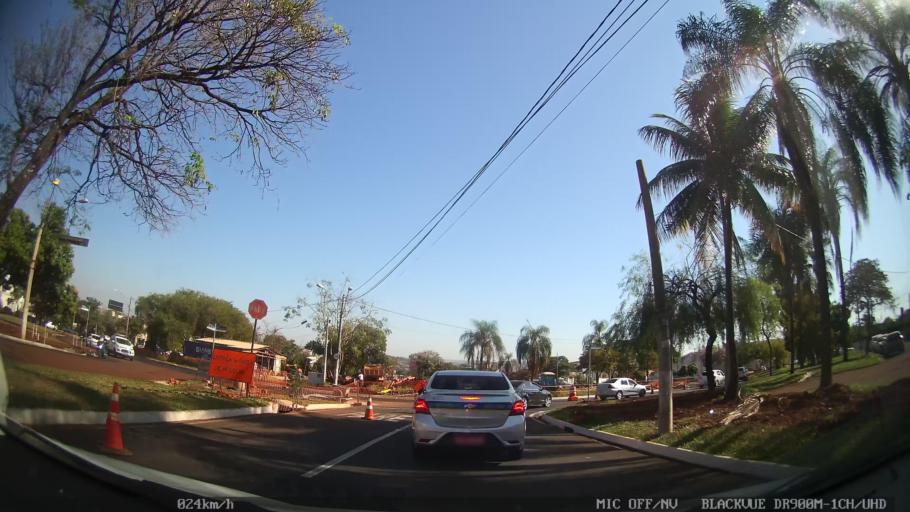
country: BR
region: Sao Paulo
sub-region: Ribeirao Preto
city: Ribeirao Preto
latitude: -21.1997
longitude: -47.8156
